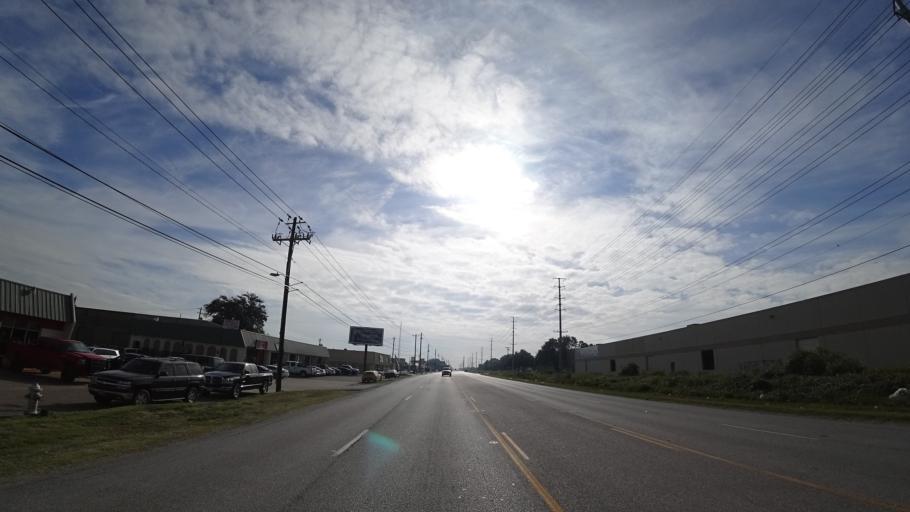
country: US
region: Texas
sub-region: Travis County
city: Austin
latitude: 30.2129
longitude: -97.7319
